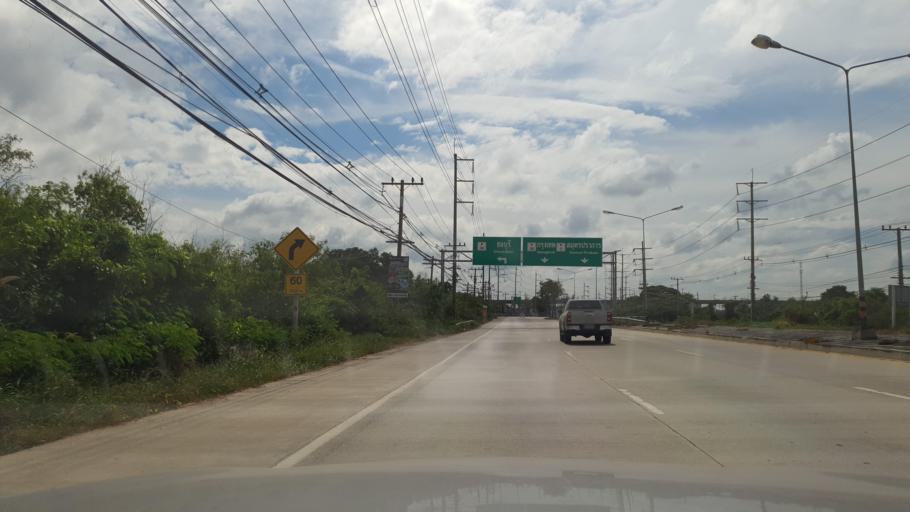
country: TH
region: Chachoengsao
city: Bang Pakong
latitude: 13.5168
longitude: 100.9911
